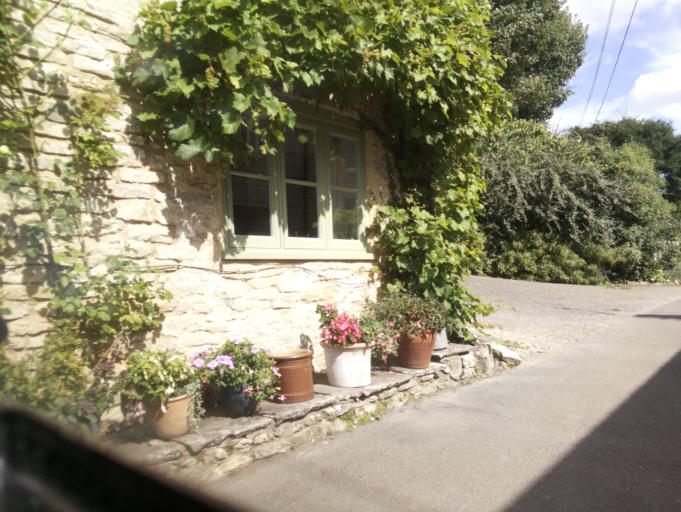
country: GB
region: England
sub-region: Gloucestershire
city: Wotton-under-Edge
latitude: 51.6448
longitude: -2.3383
